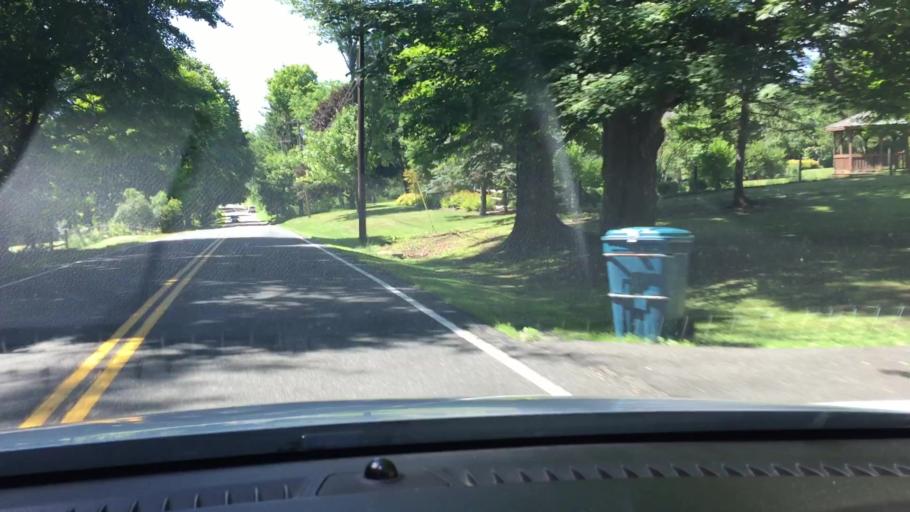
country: US
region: Massachusetts
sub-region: Berkshire County
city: Lenox
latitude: 42.3901
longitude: -73.2558
